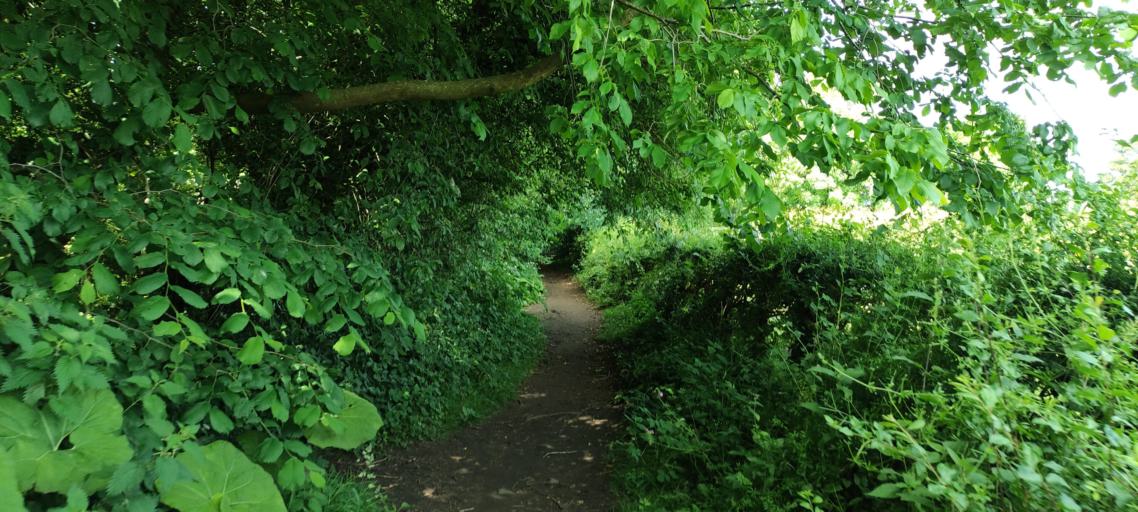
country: GB
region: England
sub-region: North Yorkshire
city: Bedale
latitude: 54.2141
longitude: -1.6534
